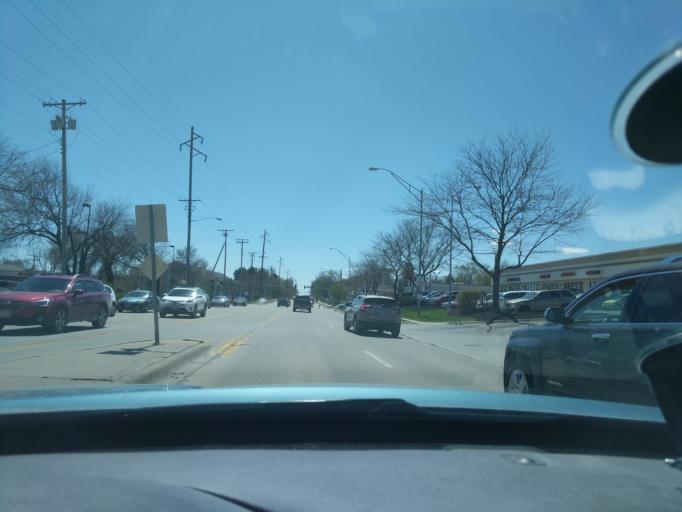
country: US
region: Nebraska
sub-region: Douglas County
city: Ralston
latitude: 41.2333
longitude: -96.1008
